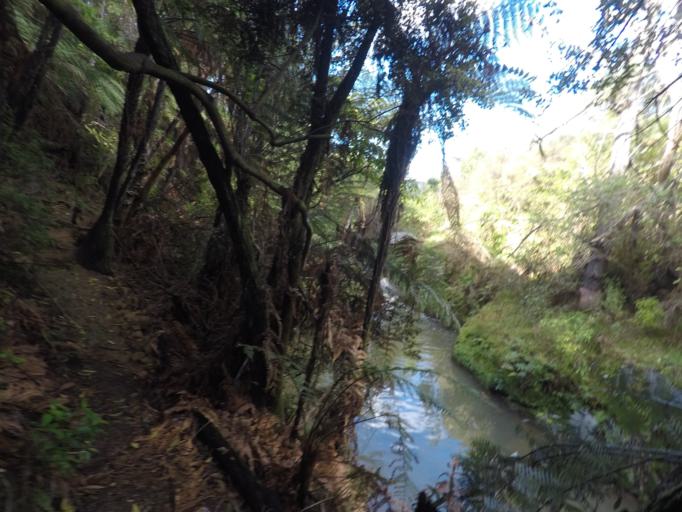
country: NZ
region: Auckland
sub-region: Auckland
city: Rothesay Bay
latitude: -36.7382
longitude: 174.7148
